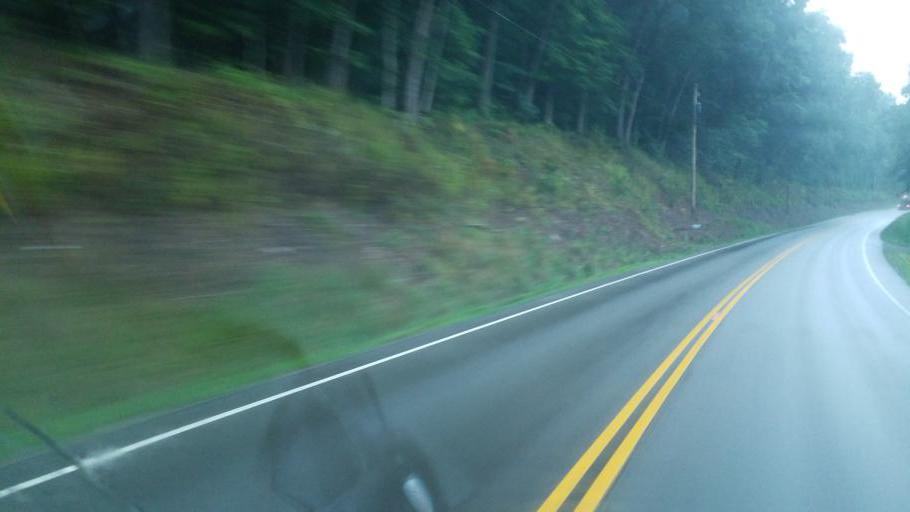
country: US
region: Ohio
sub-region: Coshocton County
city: Coshocton
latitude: 40.3397
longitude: -82.0152
